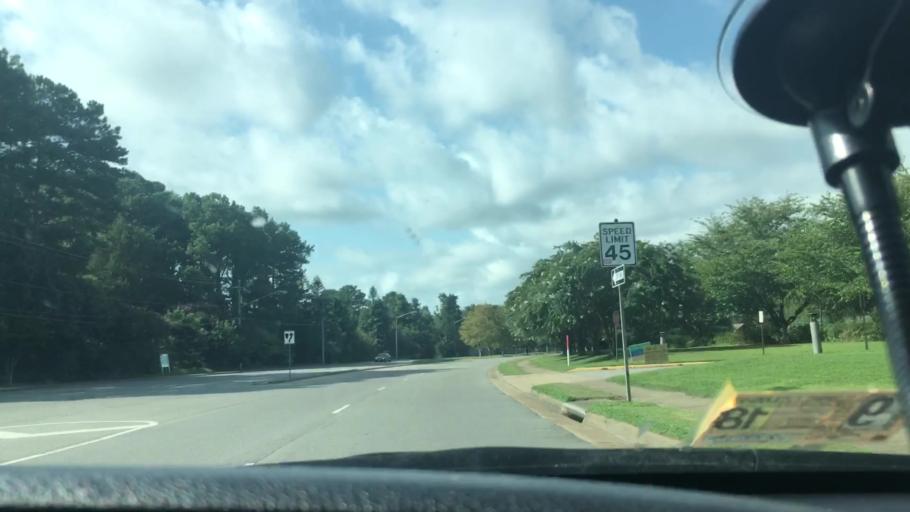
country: US
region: Virginia
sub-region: City of Virginia Beach
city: Virginia Beach
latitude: 36.8728
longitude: -76.0399
